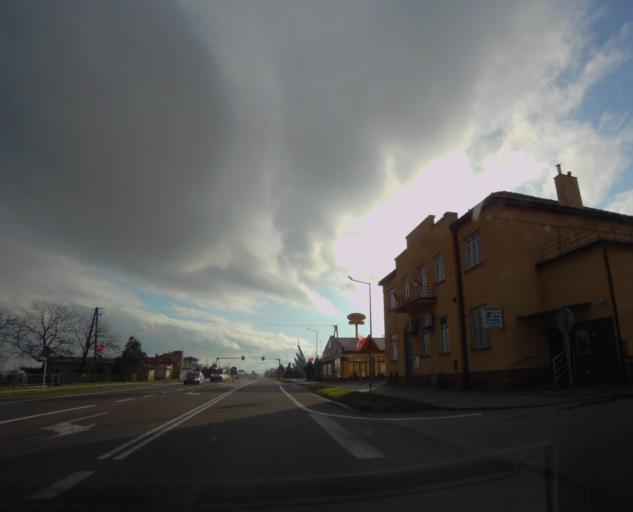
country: PL
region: Subcarpathian Voivodeship
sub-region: Powiat przemyski
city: Orly
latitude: 49.8752
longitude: 22.8122
